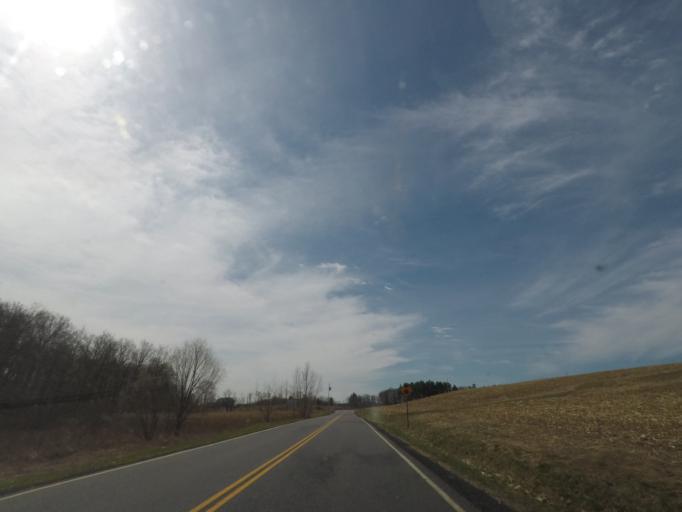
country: US
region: New York
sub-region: Saratoga County
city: Mechanicville
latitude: 42.9036
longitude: -73.7369
